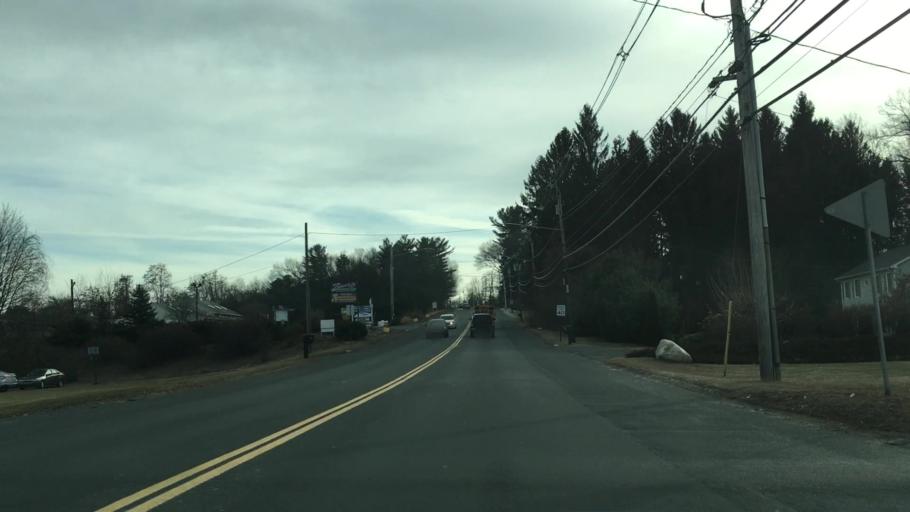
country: US
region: Massachusetts
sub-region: Hampden County
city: Westfield
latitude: 42.1084
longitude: -72.7647
